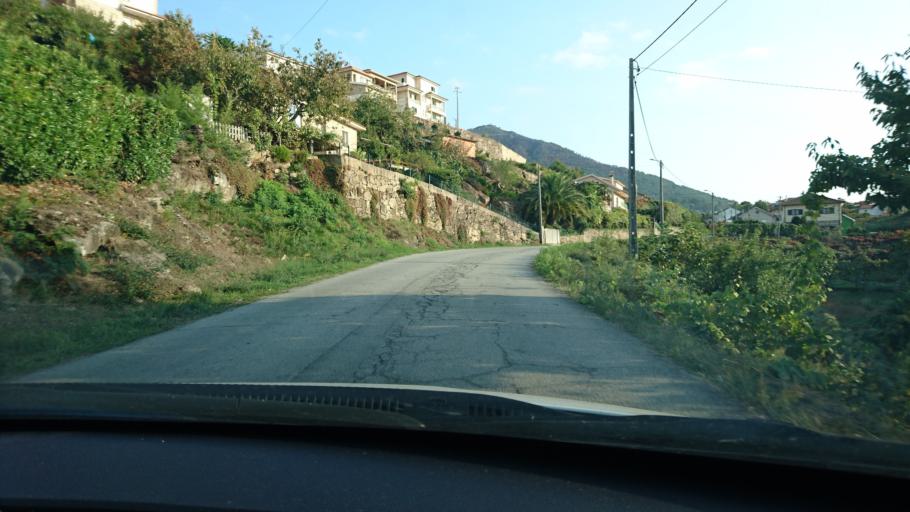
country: PT
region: Vila Real
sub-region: Mondim de Basto
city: Mondim de Basto
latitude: 41.4403
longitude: -7.9268
